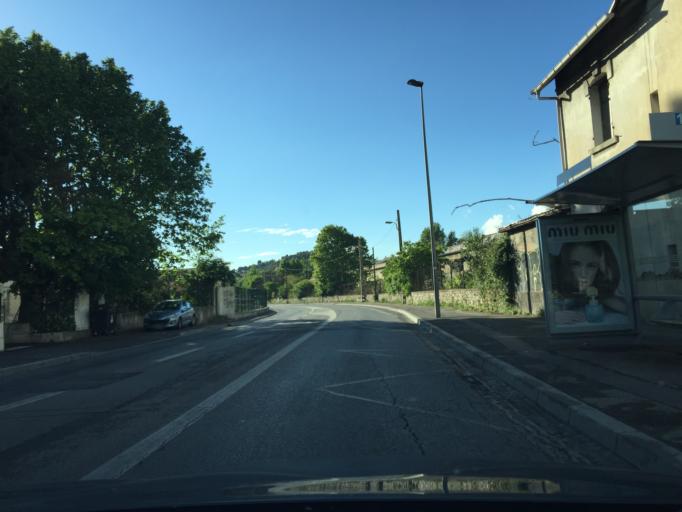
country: FR
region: Provence-Alpes-Cote d'Azur
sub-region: Departement des Bouches-du-Rhone
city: Marseille 11
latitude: 43.2907
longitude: 5.4629
